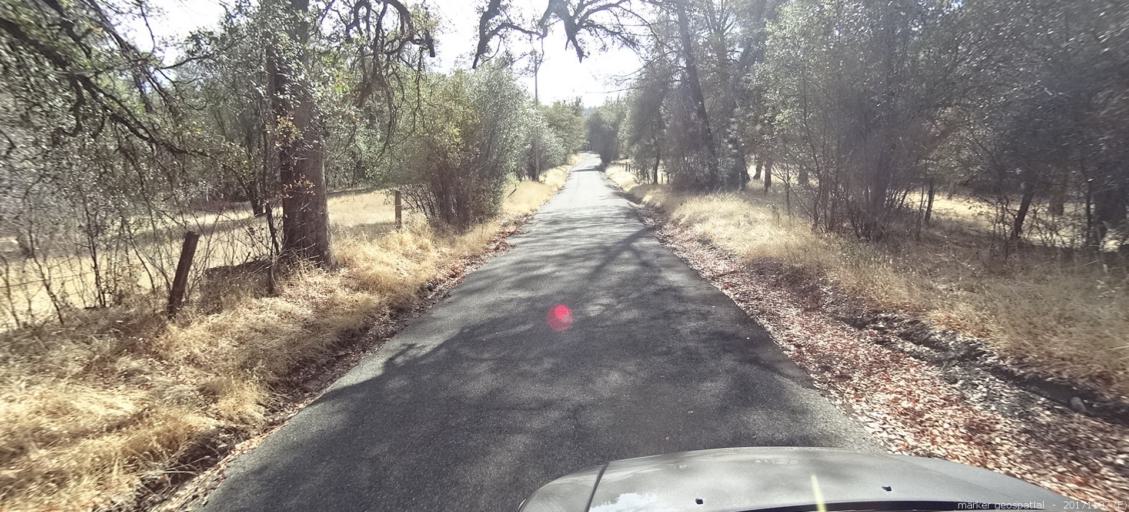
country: US
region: California
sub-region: Shasta County
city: Shasta
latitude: 40.5254
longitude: -122.5557
